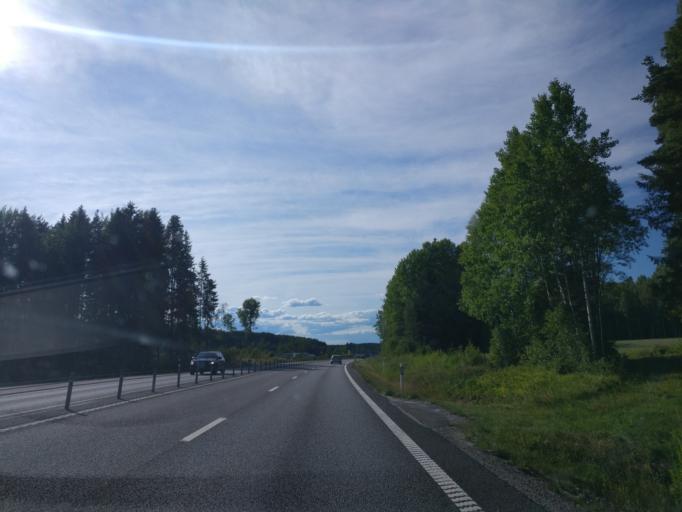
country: SE
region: Vaermland
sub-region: Arvika Kommun
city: Arvika
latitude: 59.6550
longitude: 12.6528
